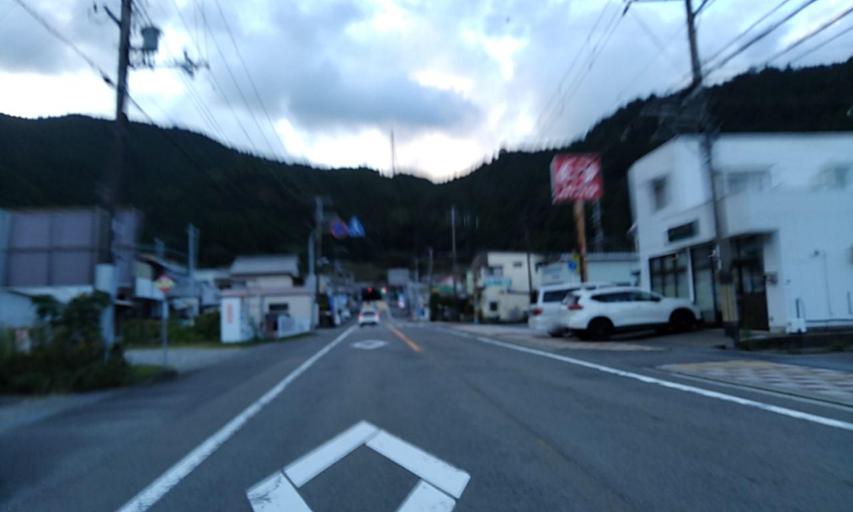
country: JP
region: Wakayama
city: Shingu
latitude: 33.7191
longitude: 135.9828
